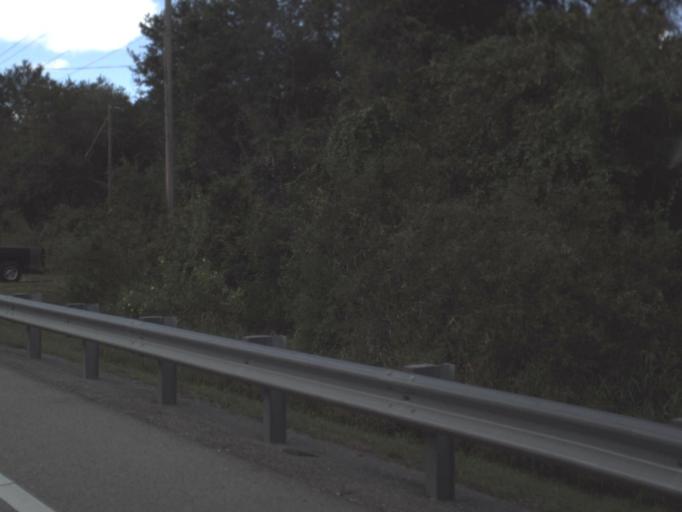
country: US
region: Florida
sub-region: Sarasota County
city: Lake Sarasota
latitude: 27.3562
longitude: -82.1806
